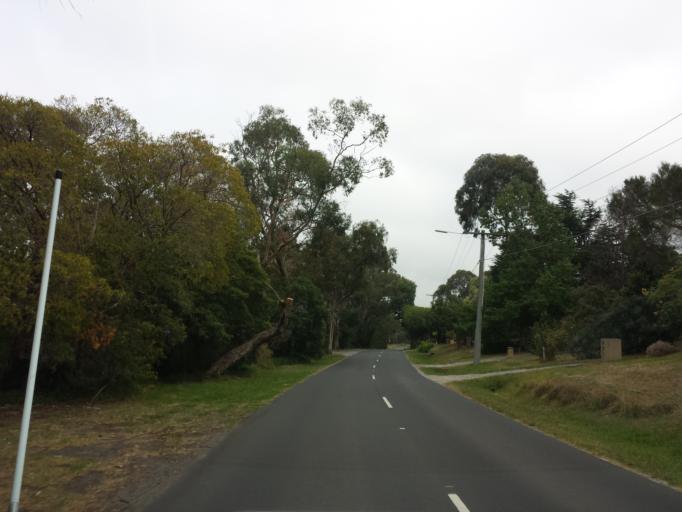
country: AU
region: Victoria
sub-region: Yarra Ranges
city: Lilydale
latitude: -37.7623
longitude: 145.3640
